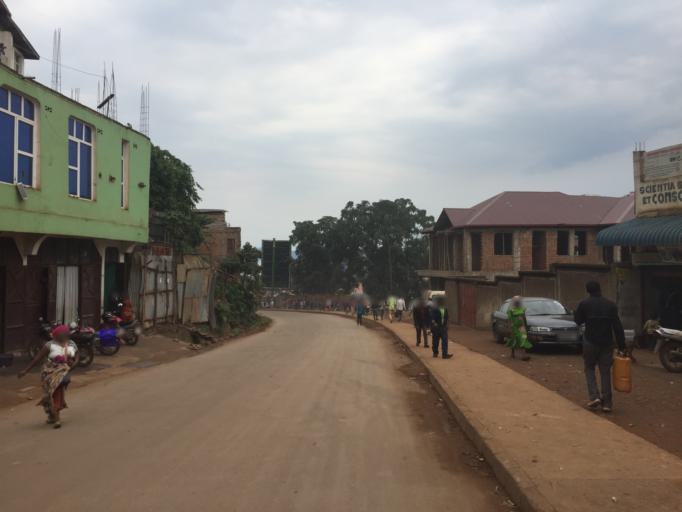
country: CD
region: South Kivu
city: Bukavu
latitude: -2.5027
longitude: 28.8512
